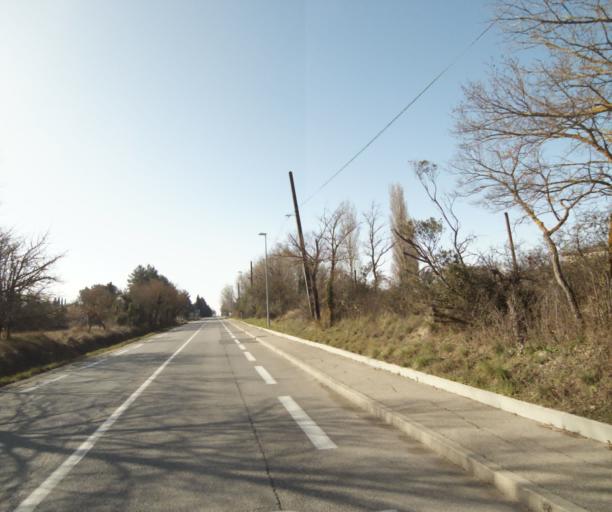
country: FR
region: Provence-Alpes-Cote d'Azur
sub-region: Departement des Bouches-du-Rhone
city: Aix-en-Provence
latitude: 43.5525
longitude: 5.4578
